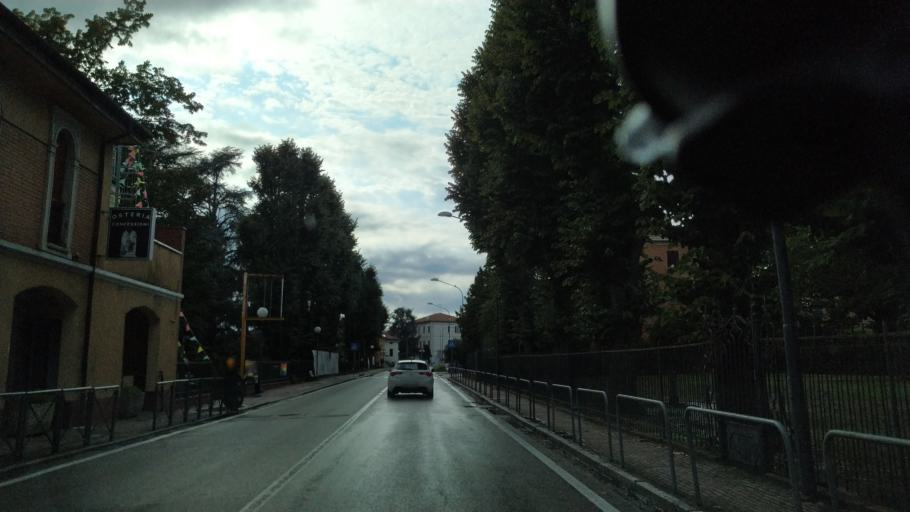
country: IT
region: Emilia-Romagna
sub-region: Provincia di Ferrara
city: Sant'Agostino
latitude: 44.7925
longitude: 11.3858
